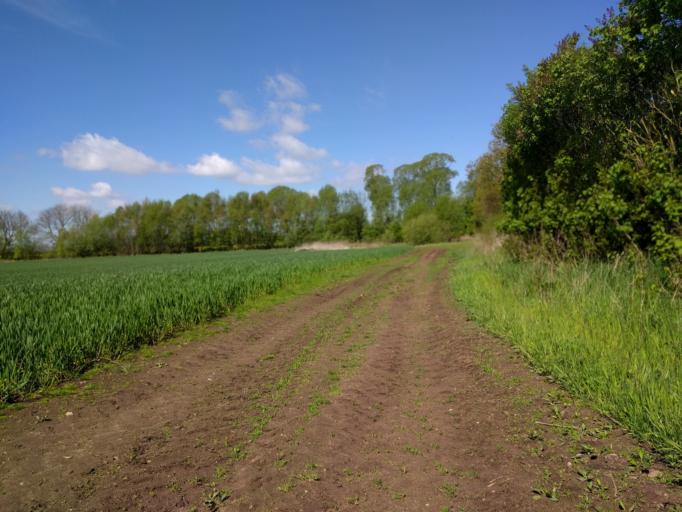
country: DK
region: South Denmark
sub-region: Kerteminde Kommune
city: Langeskov
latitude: 55.3848
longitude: 10.5522
